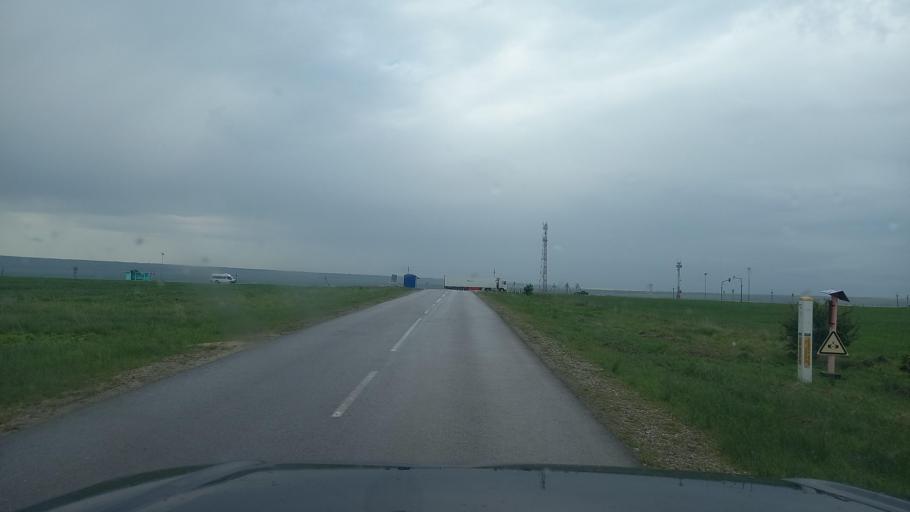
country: RU
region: Stavropol'skiy
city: Nevinnomyssk
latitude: 44.5877
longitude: 42.2227
